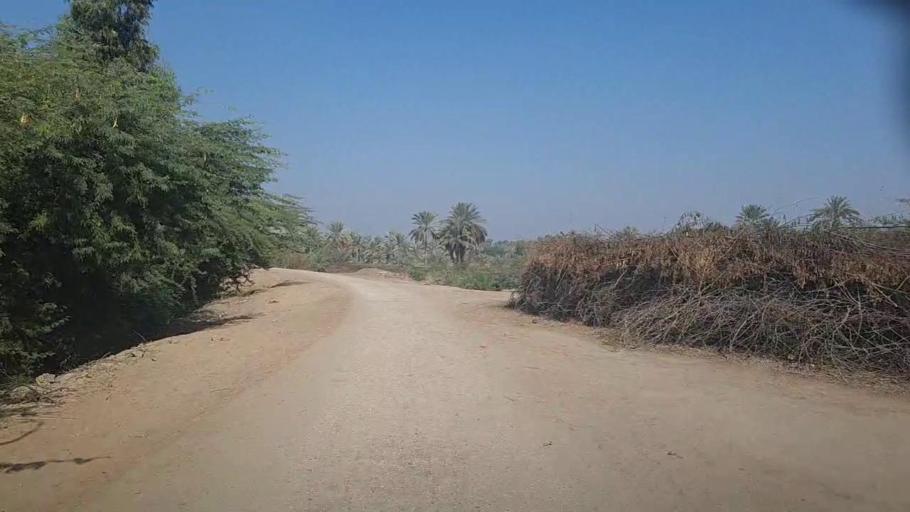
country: PK
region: Sindh
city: Kot Diji
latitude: 27.4184
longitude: 68.7062
